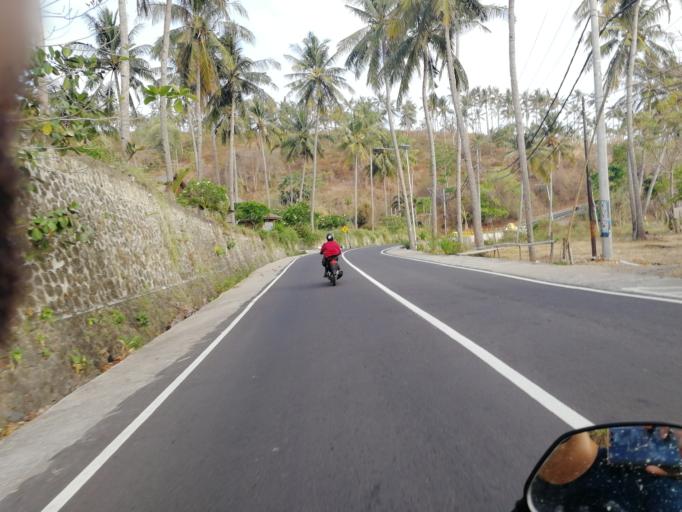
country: ID
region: West Nusa Tenggara
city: Karangsubagan
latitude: -8.4625
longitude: 116.0363
